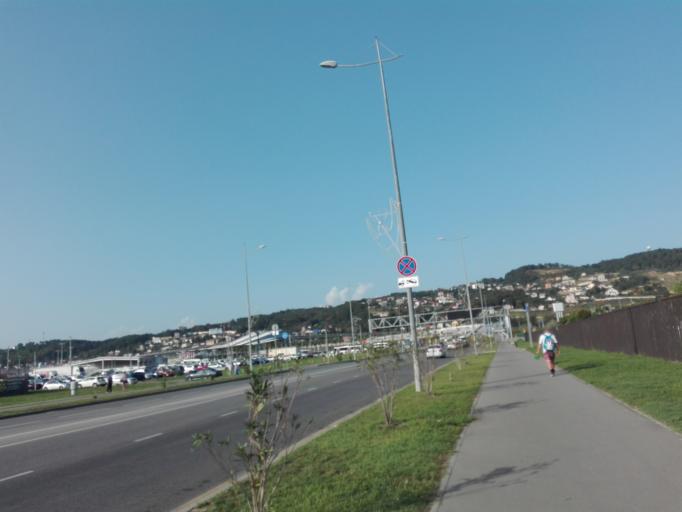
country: RU
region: Krasnodarskiy
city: Adler
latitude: 43.4050
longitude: 39.9723
